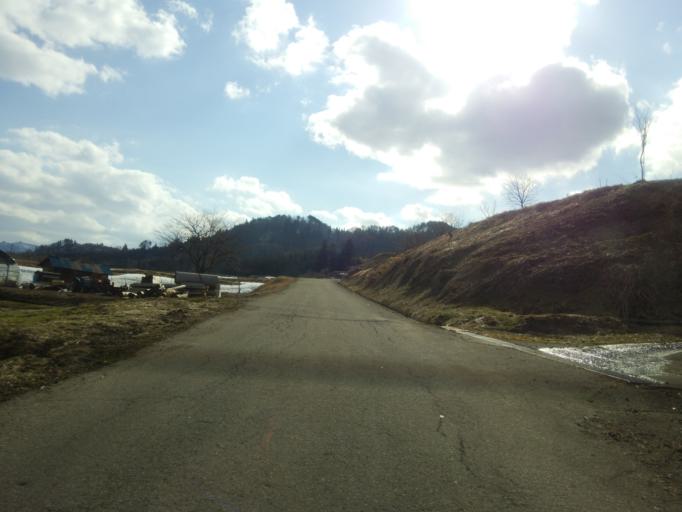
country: JP
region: Fukushima
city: Kitakata
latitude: 37.4515
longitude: 139.8031
